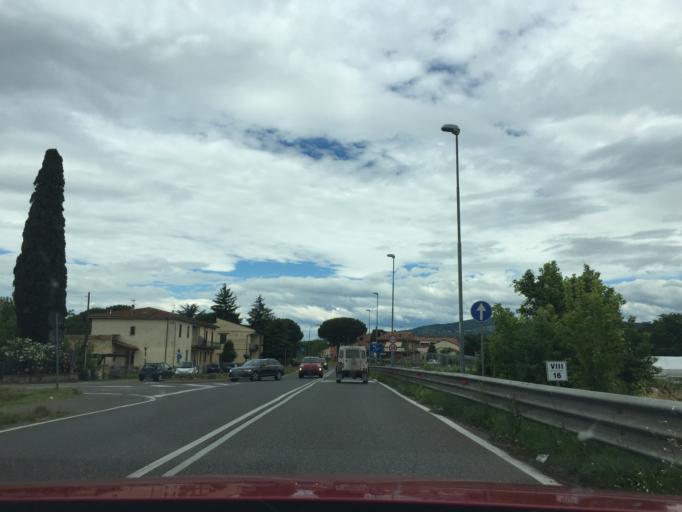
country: IT
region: Tuscany
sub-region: Province of Florence
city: Montelupo Fiorentino
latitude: 43.7276
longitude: 11.0231
